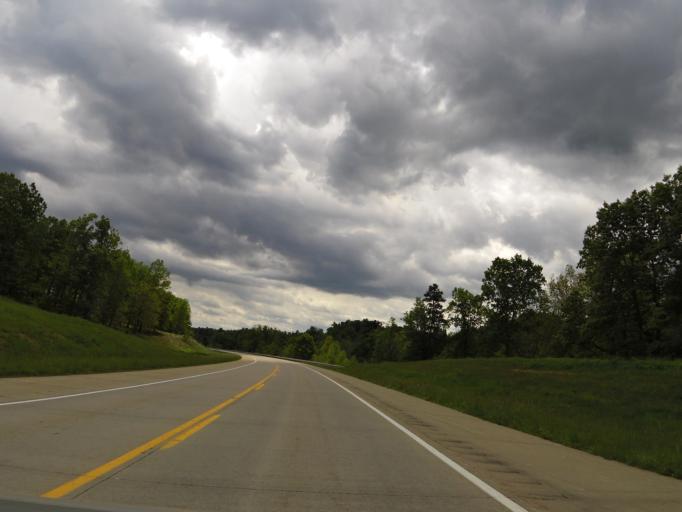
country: US
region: West Virginia
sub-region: Mason County
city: New Haven
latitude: 38.9816
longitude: -81.8682
